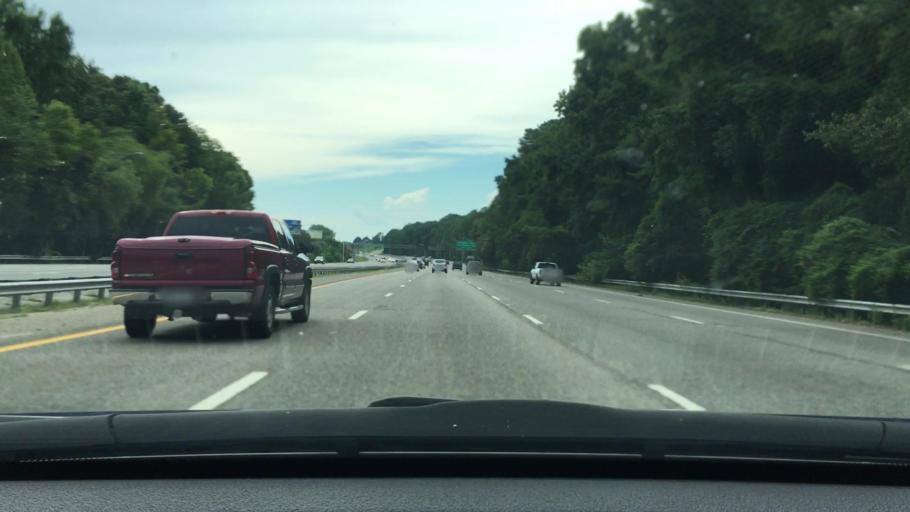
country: US
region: South Carolina
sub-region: Lexington County
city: West Columbia
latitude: 34.0106
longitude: -81.0643
